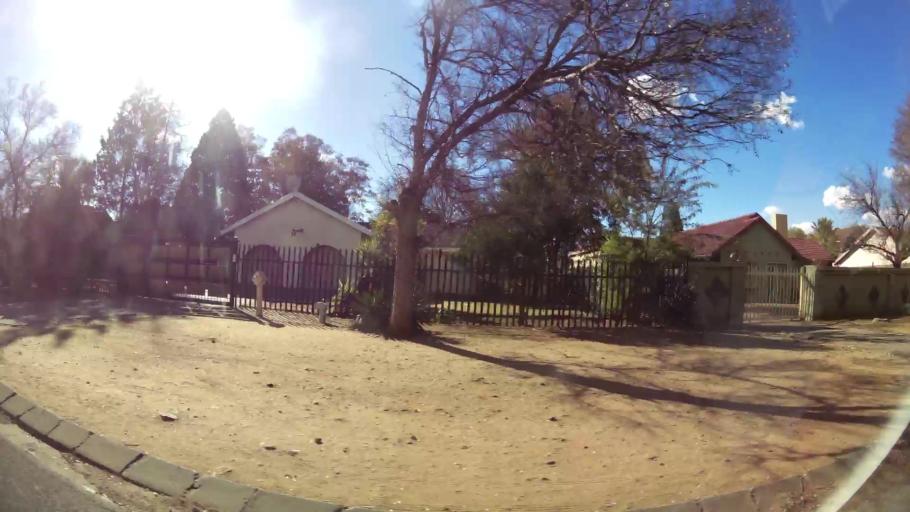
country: ZA
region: North-West
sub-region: Dr Kenneth Kaunda District Municipality
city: Klerksdorp
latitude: -26.8245
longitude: 26.6637
